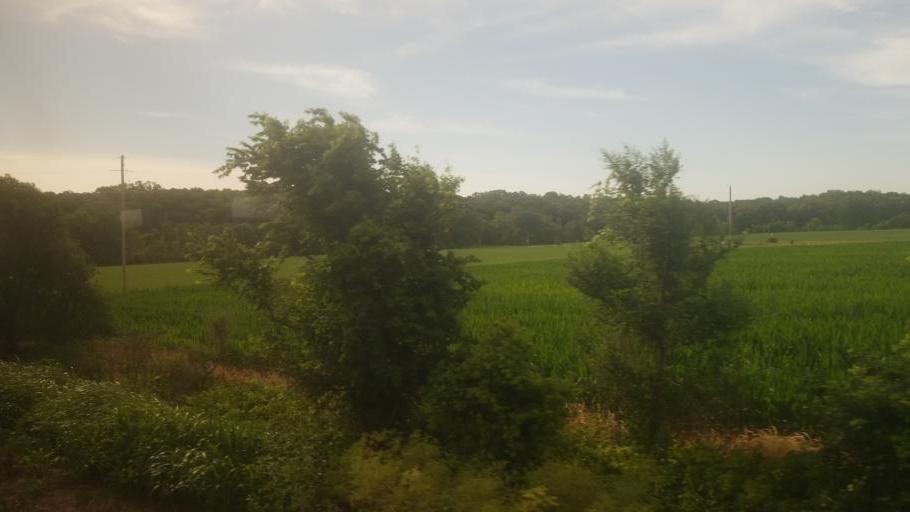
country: US
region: Kansas
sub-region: Douglas County
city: Eudora
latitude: 38.9657
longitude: -95.0574
